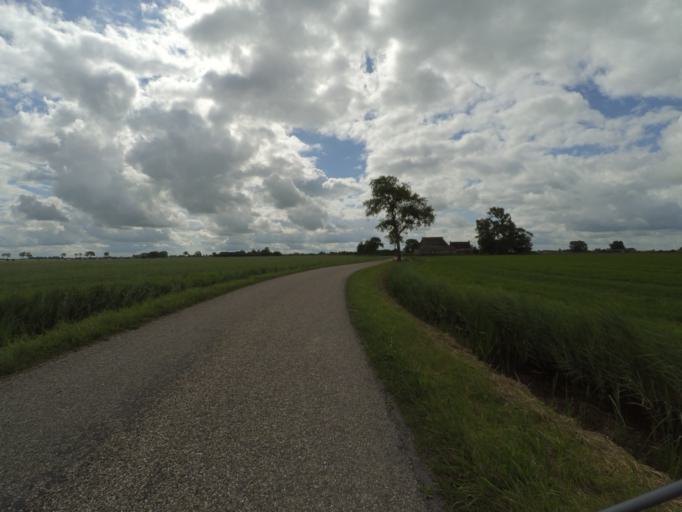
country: NL
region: Friesland
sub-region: Gemeente Kollumerland en Nieuwkruisland
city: Kollum
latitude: 53.2843
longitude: 6.2262
